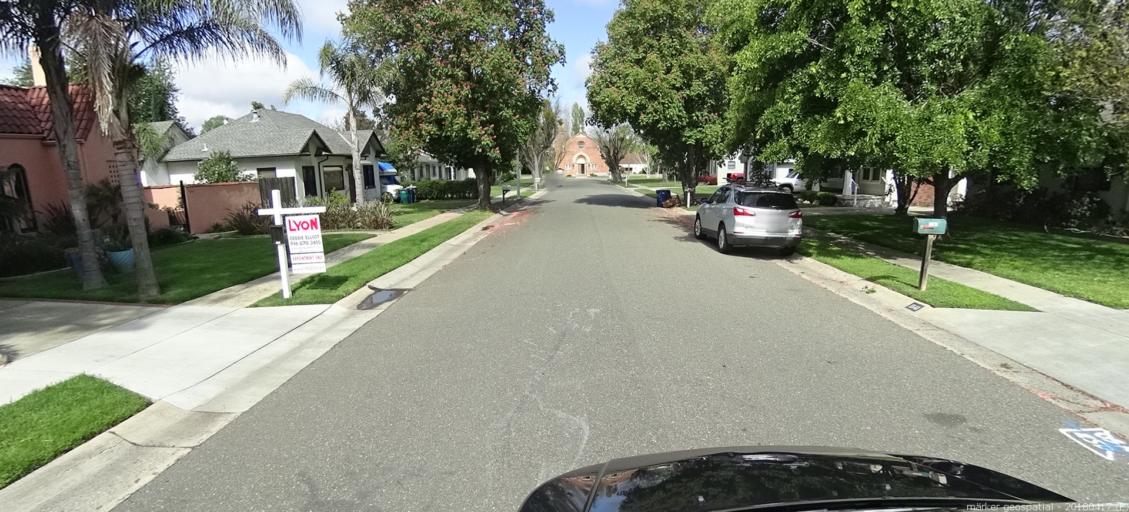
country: US
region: California
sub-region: Sacramento County
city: Walnut Grove
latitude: 38.2466
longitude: -121.5144
